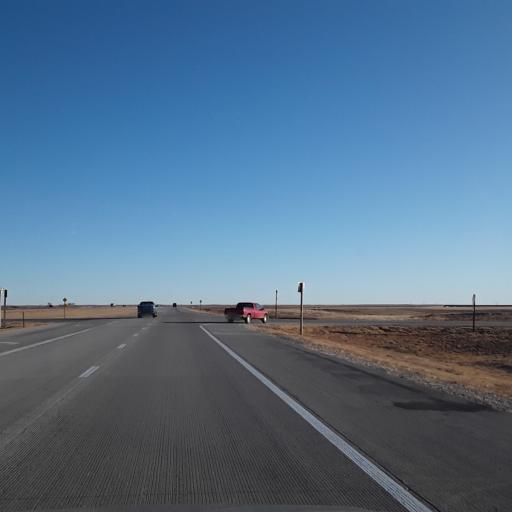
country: US
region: Kansas
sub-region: Seward County
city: Liberal
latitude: 37.1029
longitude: -100.7966
